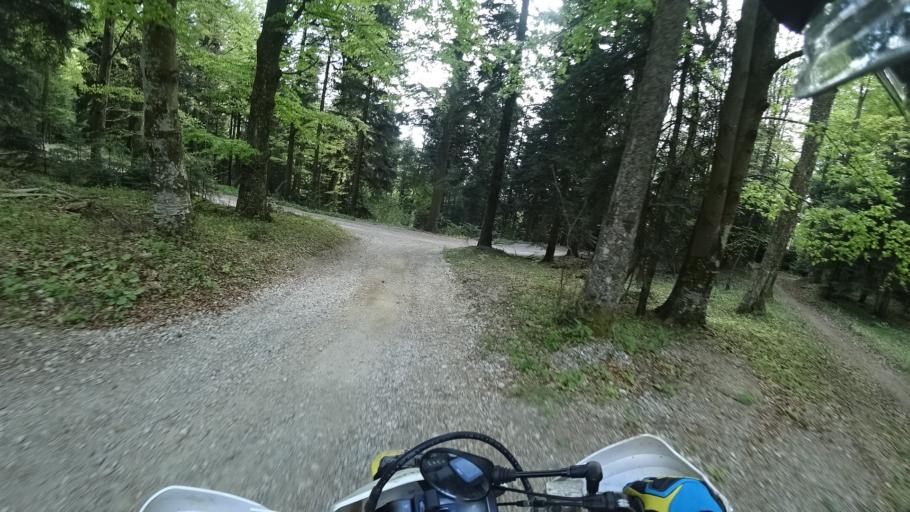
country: HR
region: Grad Zagreb
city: Kasina
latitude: 45.9089
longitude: 15.9442
